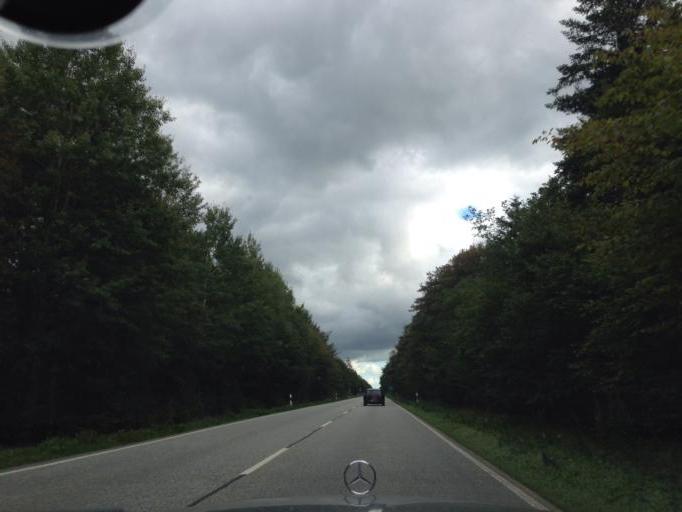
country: DE
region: Schleswig-Holstein
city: Leck
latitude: 54.7502
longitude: 9.0141
